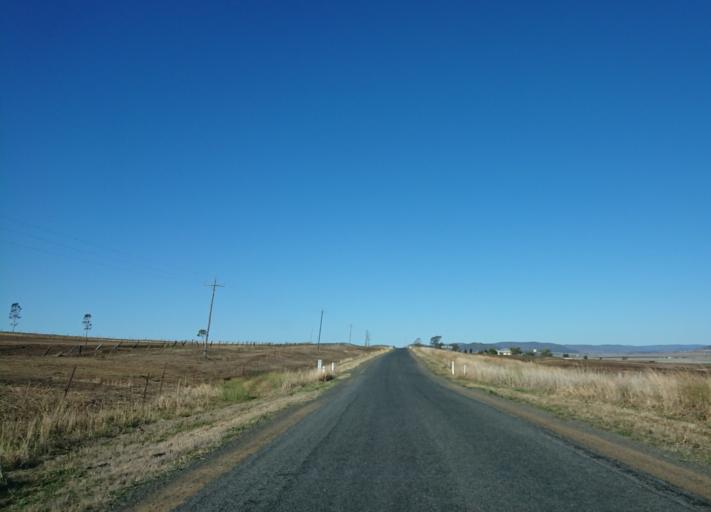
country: AU
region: Queensland
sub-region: Toowoomba
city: Top Camp
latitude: -27.8097
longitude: 151.9607
